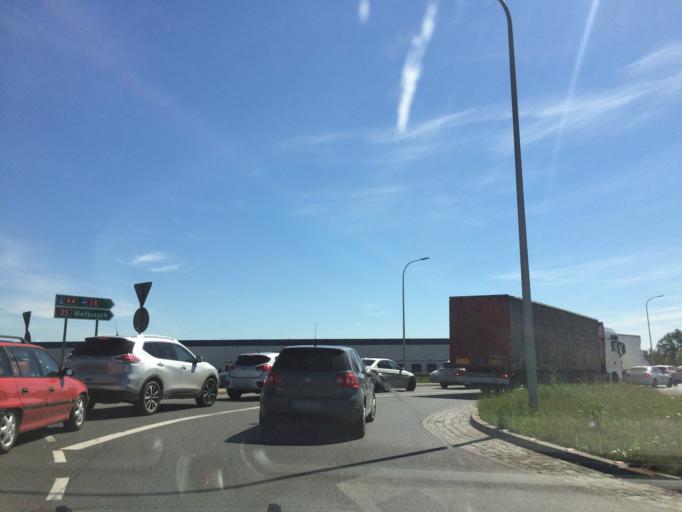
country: PL
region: Lower Silesian Voivodeship
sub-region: Powiat wroclawski
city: Bielany Wroclawskie
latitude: 51.0418
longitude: 16.9484
